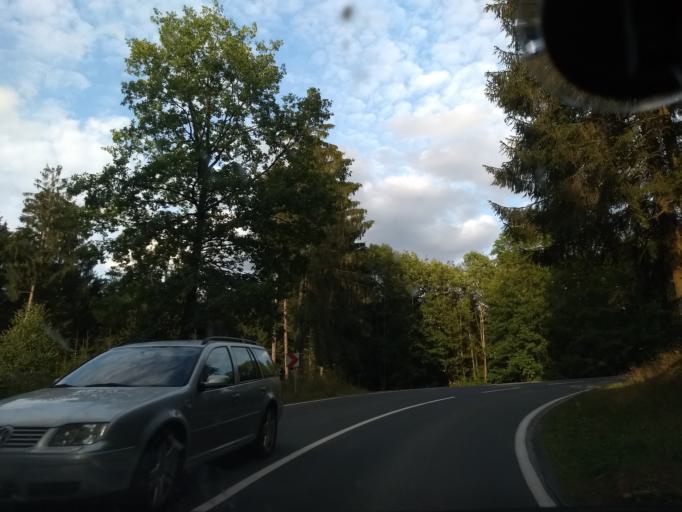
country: DE
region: North Rhine-Westphalia
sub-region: Regierungsbezirk Arnsberg
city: Arnsberg
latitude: 51.3549
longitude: 8.0694
